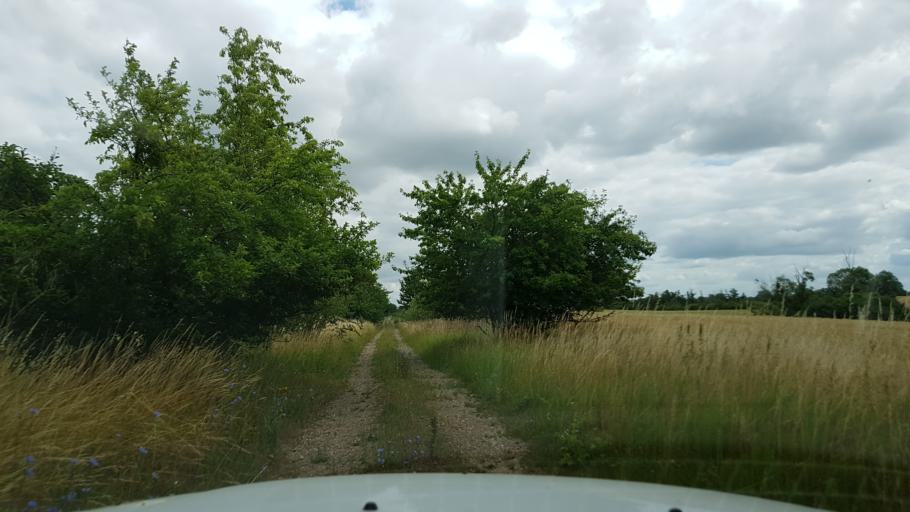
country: PL
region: West Pomeranian Voivodeship
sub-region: Powiat mysliborski
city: Mysliborz
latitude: 52.9416
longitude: 14.9240
